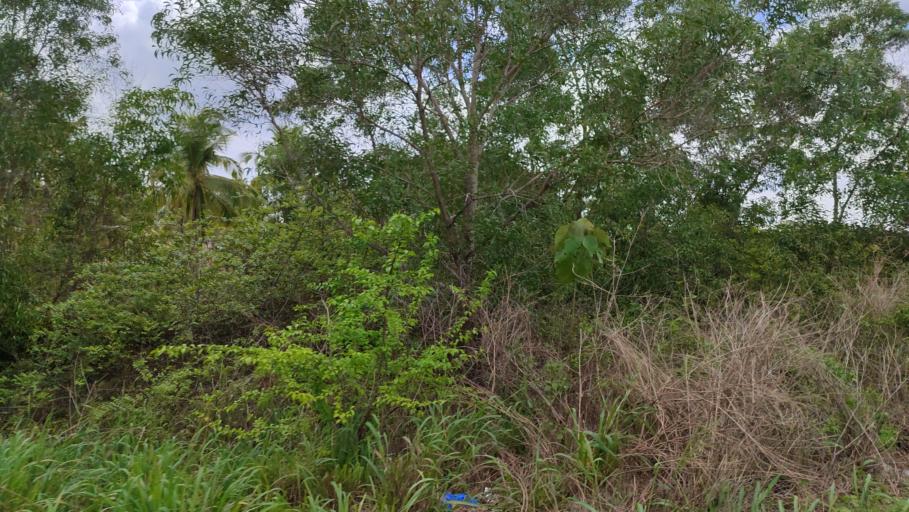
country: IN
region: Kerala
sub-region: Kasaragod District
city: Kannangad
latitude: 12.3903
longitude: 75.1016
